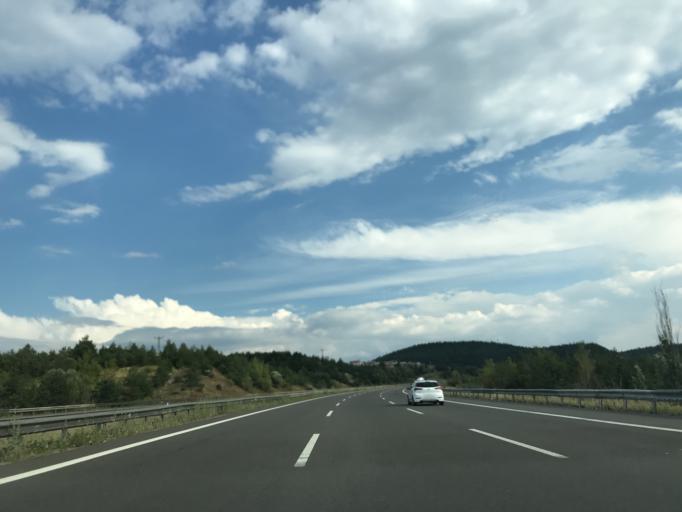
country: TR
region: Bolu
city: Gerede
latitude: 40.6359
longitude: 32.2349
